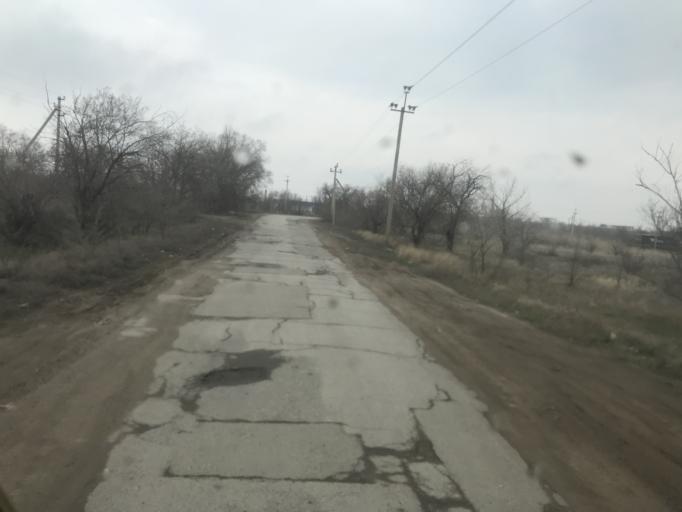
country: RU
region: Volgograd
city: Krasnoslobodsk
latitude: 48.5331
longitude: 44.6066
